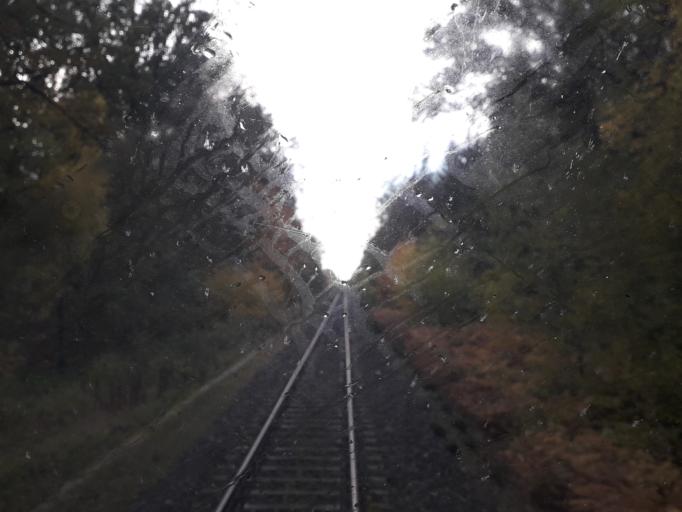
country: DE
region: Brandenburg
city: Heiligengrabe
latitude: 53.1515
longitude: 12.3494
